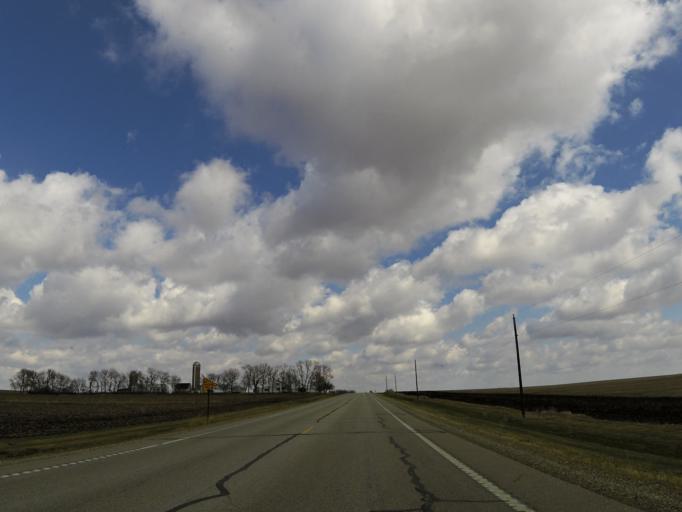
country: US
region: Minnesota
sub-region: Dodge County
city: Mantorville
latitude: 44.0803
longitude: -92.8060
